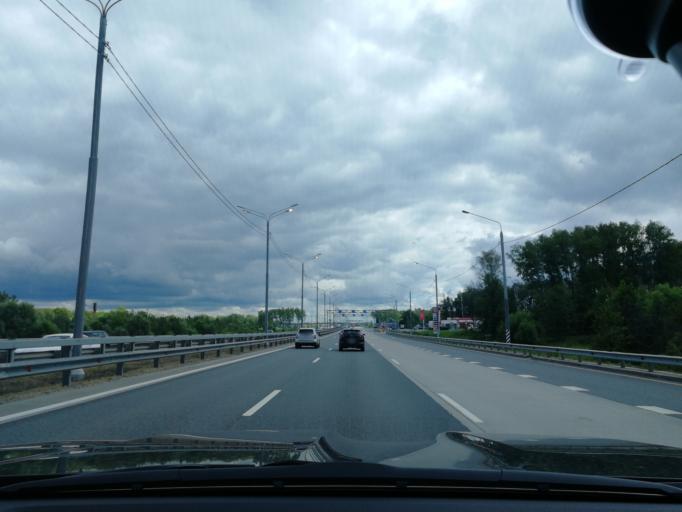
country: RU
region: Moskovskaya
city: Belyye Stolby
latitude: 55.2915
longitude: 37.8487
